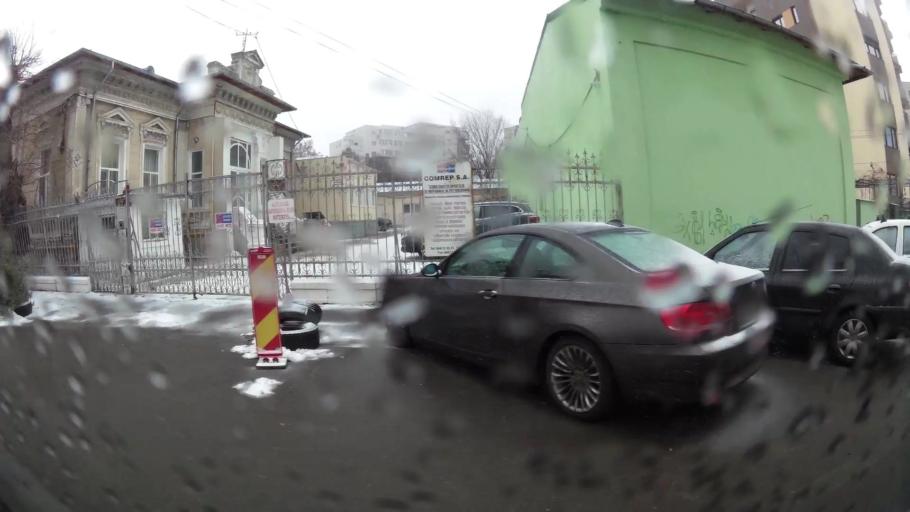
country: RO
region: Prahova
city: Ploiesti
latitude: 44.9398
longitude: 26.0188
